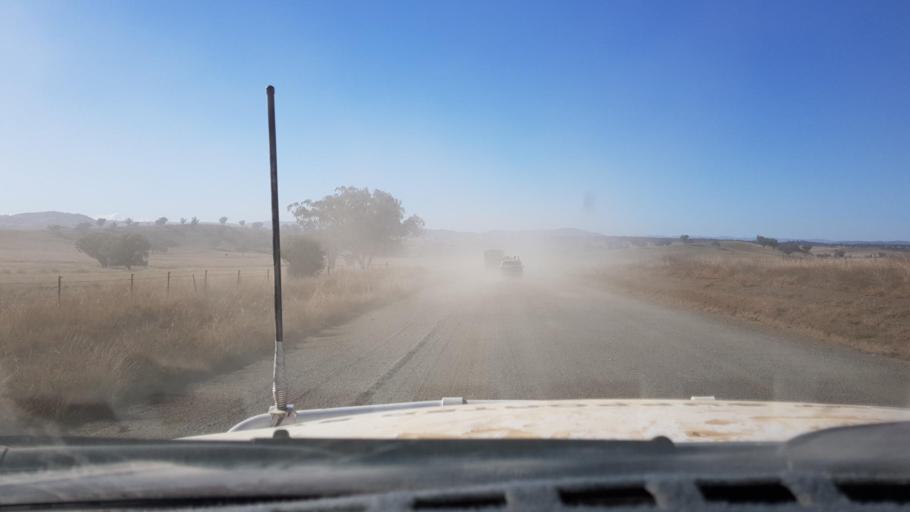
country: AU
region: New South Wales
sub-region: Narrabri
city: Blair Athol
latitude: -30.6737
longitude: 150.4074
